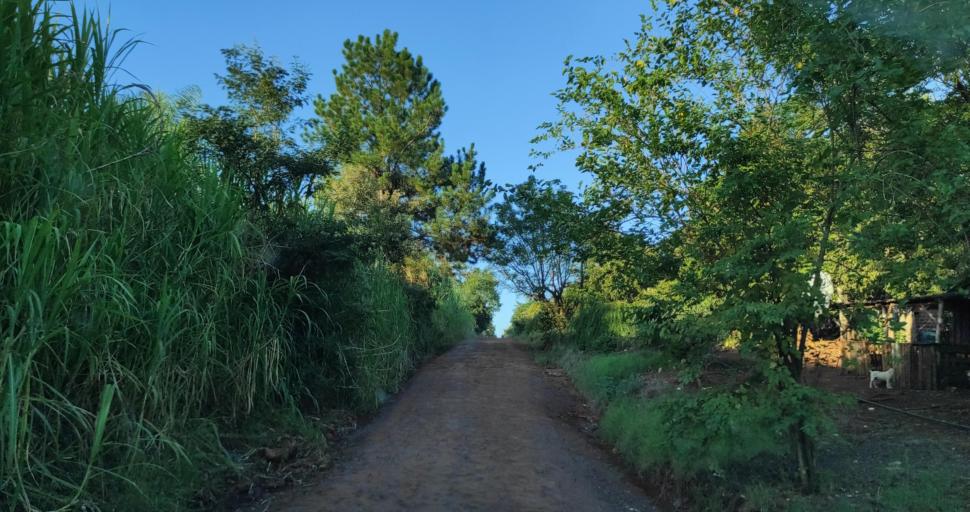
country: AR
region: Misiones
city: Gobernador Roca
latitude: -27.2179
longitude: -55.4241
